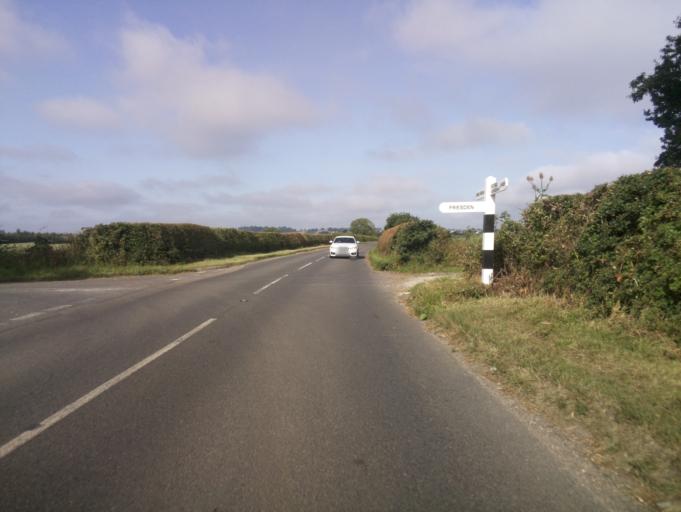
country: GB
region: England
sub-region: Borough of Swindon
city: Highworth
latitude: 51.6372
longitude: -1.6725
